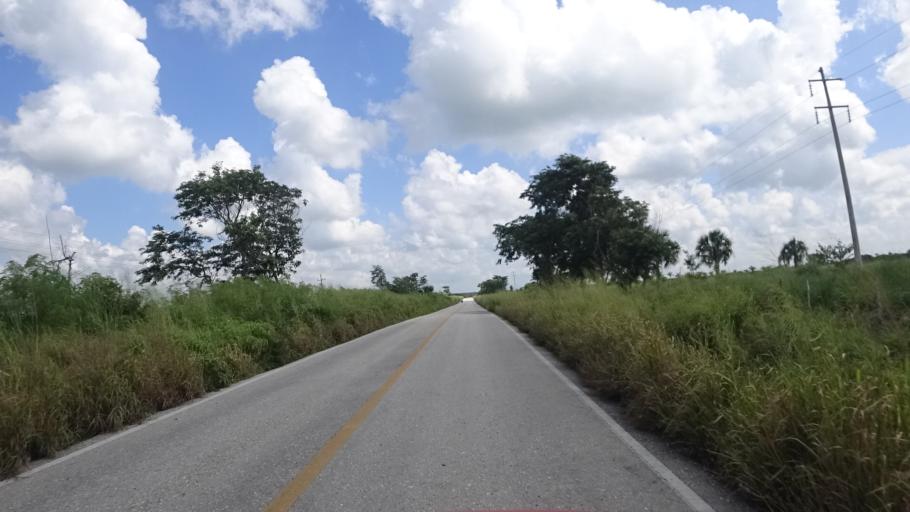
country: MX
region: Yucatan
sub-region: Panaba
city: Loche
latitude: 21.3412
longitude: -88.1569
